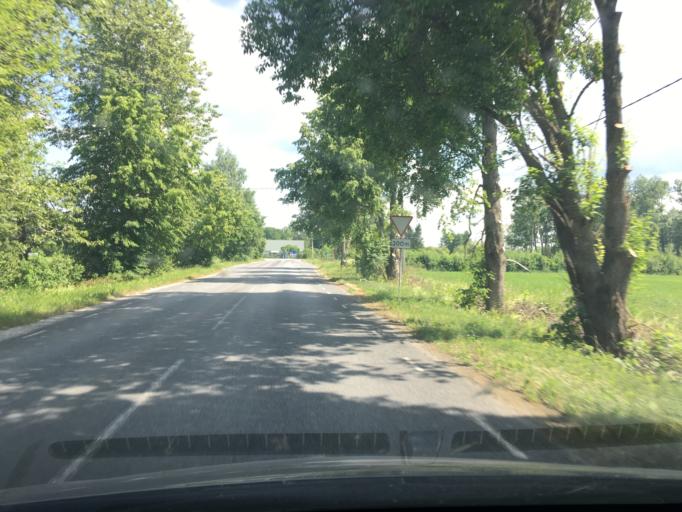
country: EE
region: Paernumaa
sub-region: Halinga vald
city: Parnu-Jaagupi
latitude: 58.7074
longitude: 24.3988
